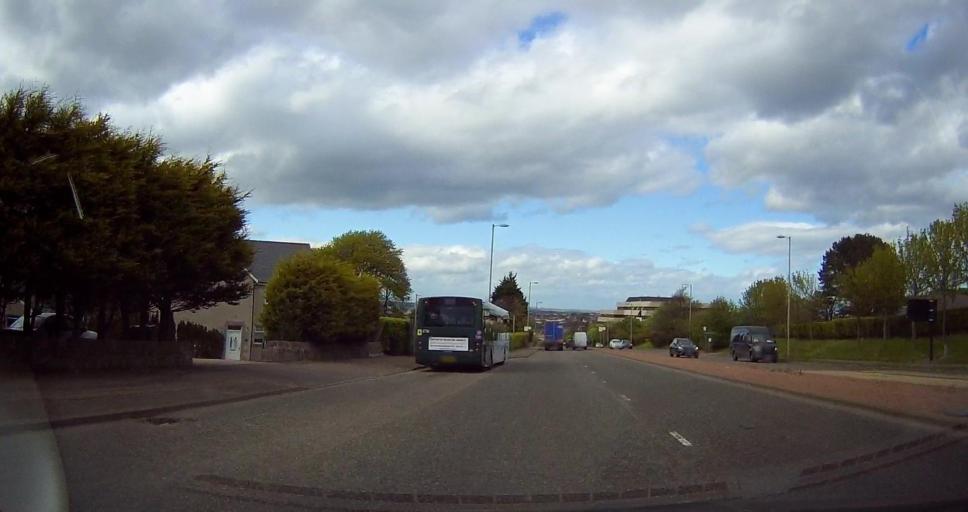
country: GB
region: Scotland
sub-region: Aberdeen City
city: Aberdeen
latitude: 57.1179
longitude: -2.0889
